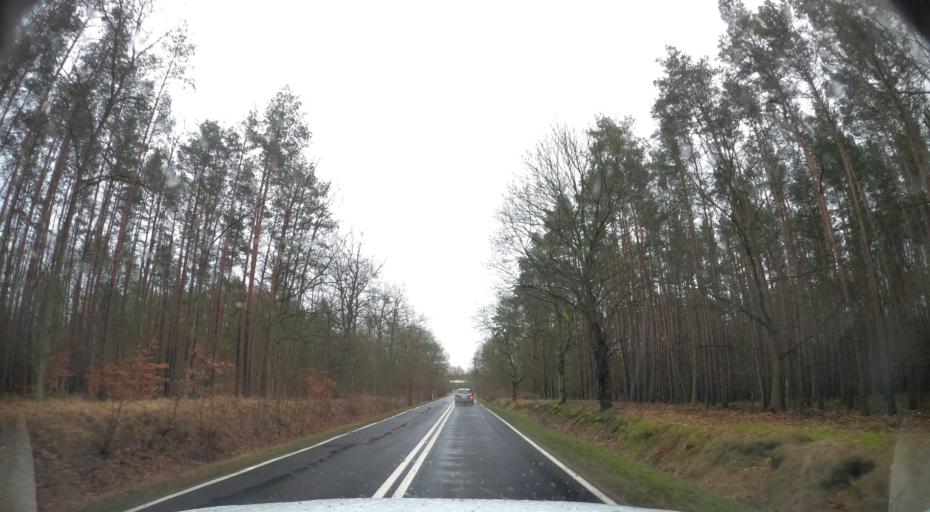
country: PL
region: West Pomeranian Voivodeship
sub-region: Powiat gryfinski
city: Stare Czarnowo
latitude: 53.3952
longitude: 14.7064
